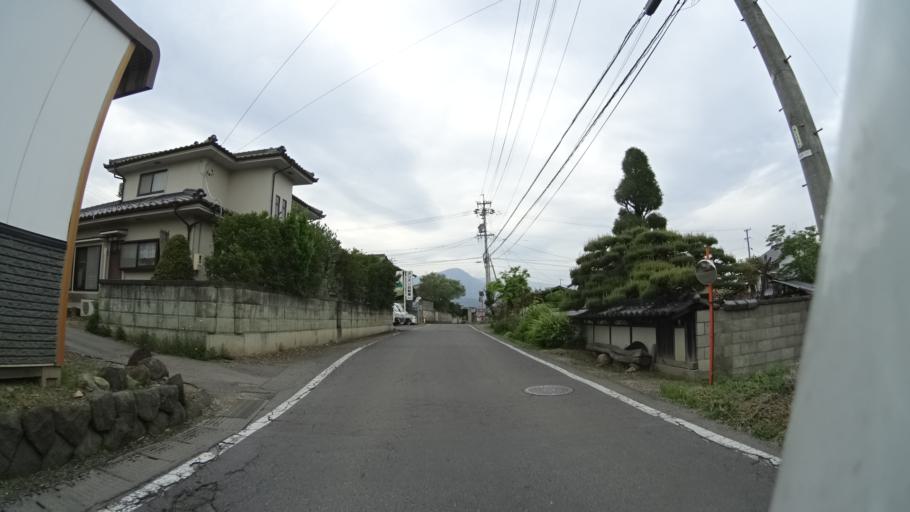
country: JP
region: Nagano
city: Kamimaruko
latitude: 36.3484
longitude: 138.2045
